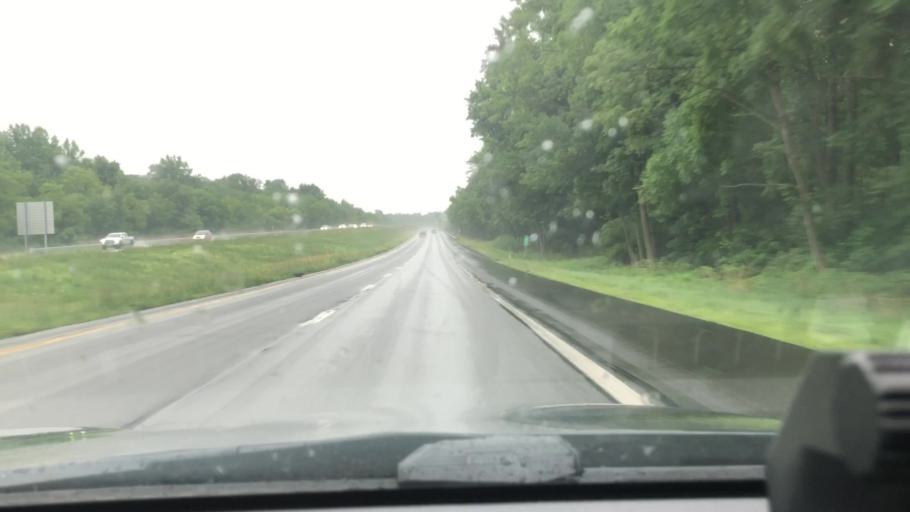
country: US
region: Pennsylvania
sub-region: Northampton County
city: Belfast
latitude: 40.8042
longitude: -75.2981
